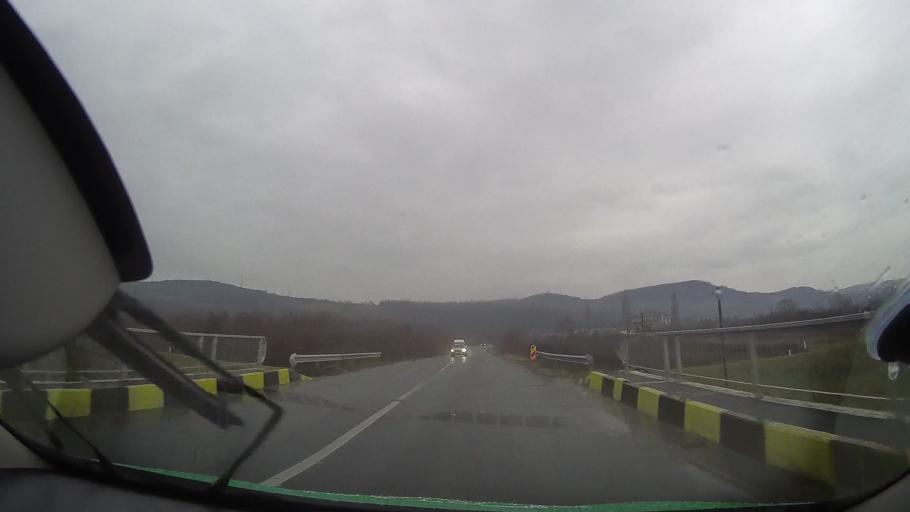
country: RO
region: Bihor
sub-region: Comuna Sambata
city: Sambata
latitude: 46.7926
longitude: 22.2038
